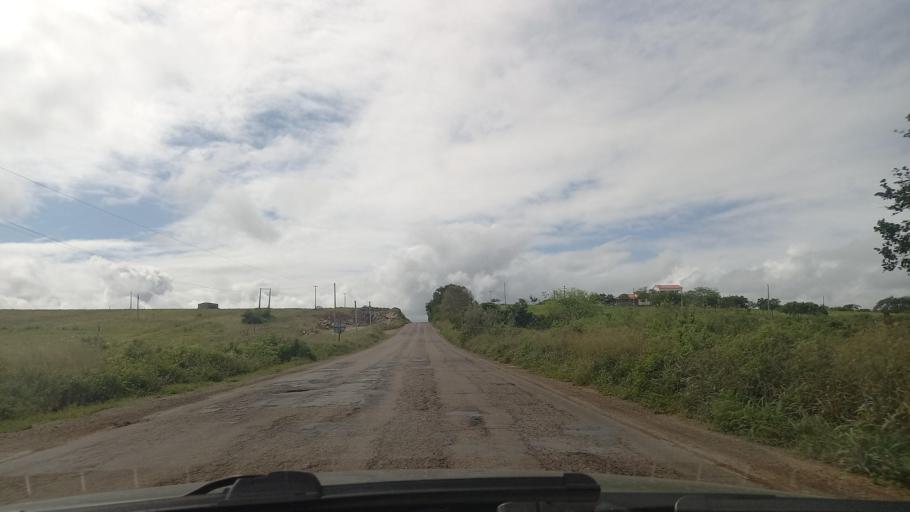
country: BR
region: Alagoas
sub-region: Batalha
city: Batalha
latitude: -9.6642
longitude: -37.1646
